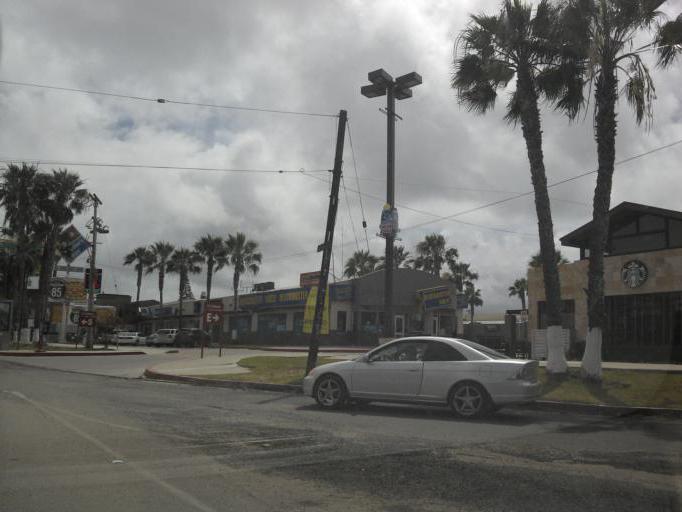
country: US
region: California
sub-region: San Diego County
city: Imperial Beach
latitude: 32.5301
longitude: -117.1163
